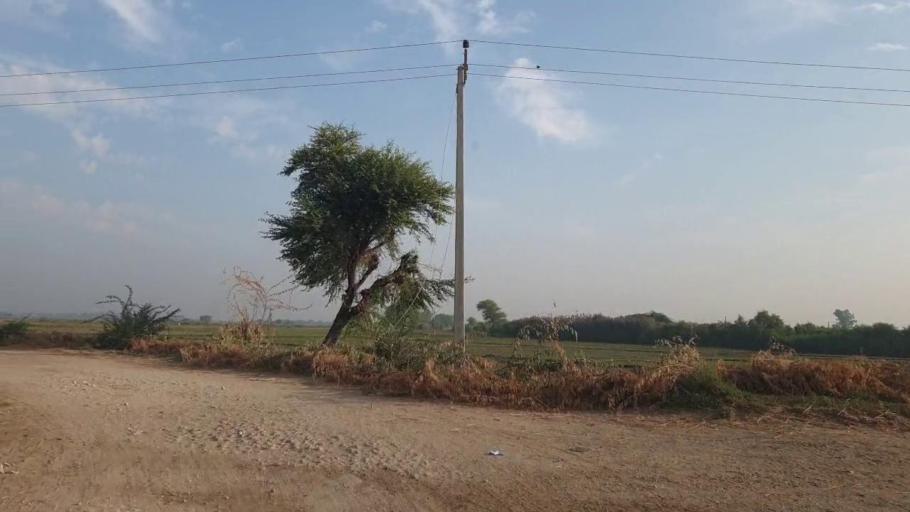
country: PK
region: Sindh
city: Tando Bago
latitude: 24.8085
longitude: 68.9576
